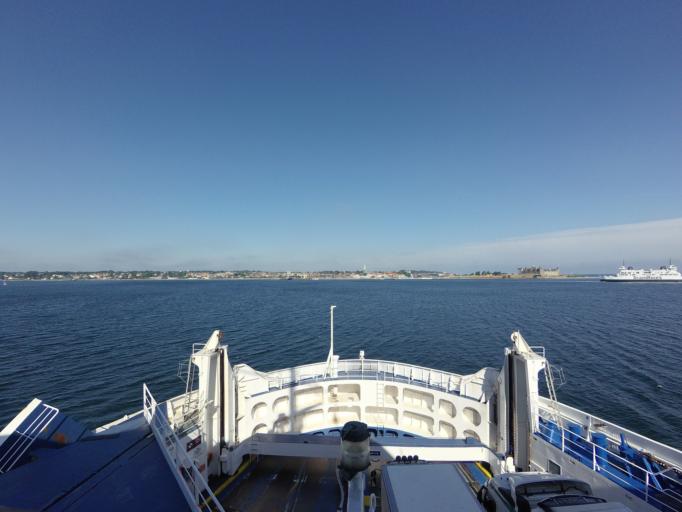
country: DK
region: Capital Region
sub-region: Helsingor Kommune
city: Helsingor
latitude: 56.0307
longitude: 12.6315
